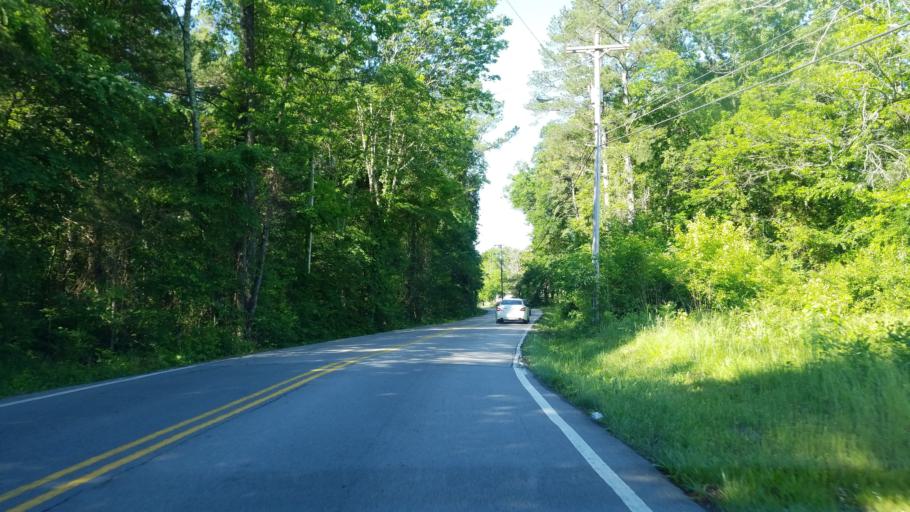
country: US
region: Tennessee
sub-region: Hamilton County
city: East Brainerd
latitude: 35.0335
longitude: -85.1339
